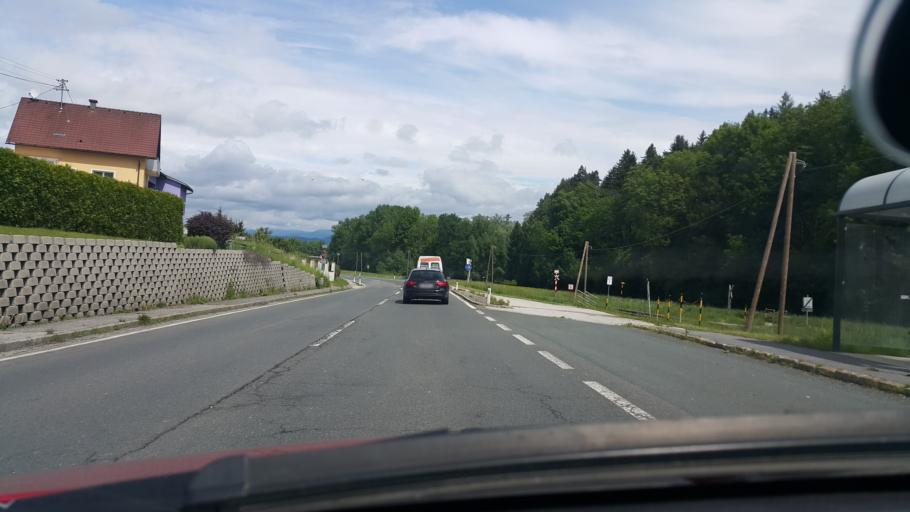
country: AT
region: Carinthia
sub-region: Politischer Bezirk Klagenfurt Land
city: Maria Rain
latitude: 46.5749
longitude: 14.2860
